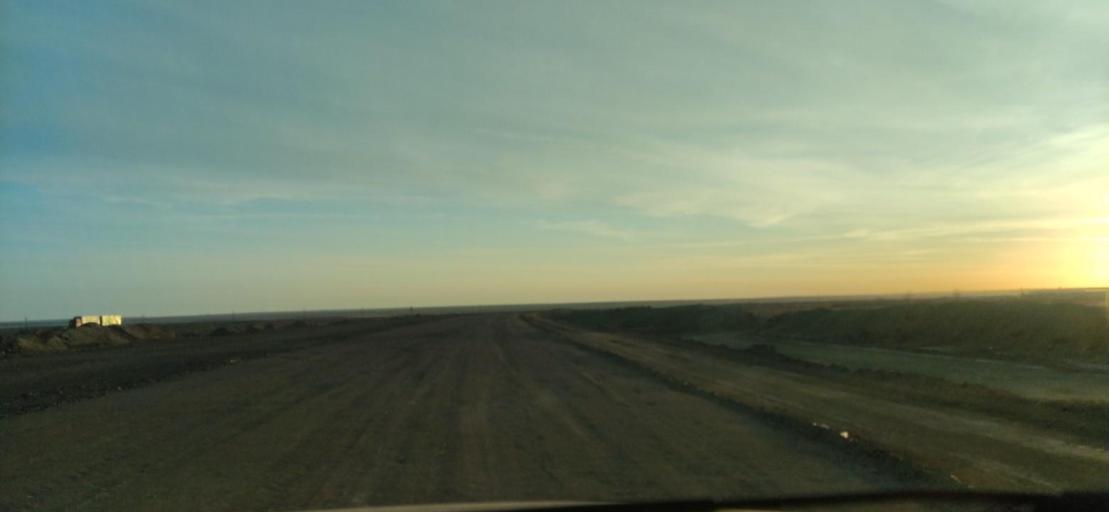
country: KZ
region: Qaraghandy
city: Saryshaghan
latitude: 46.0132
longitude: 73.5885
